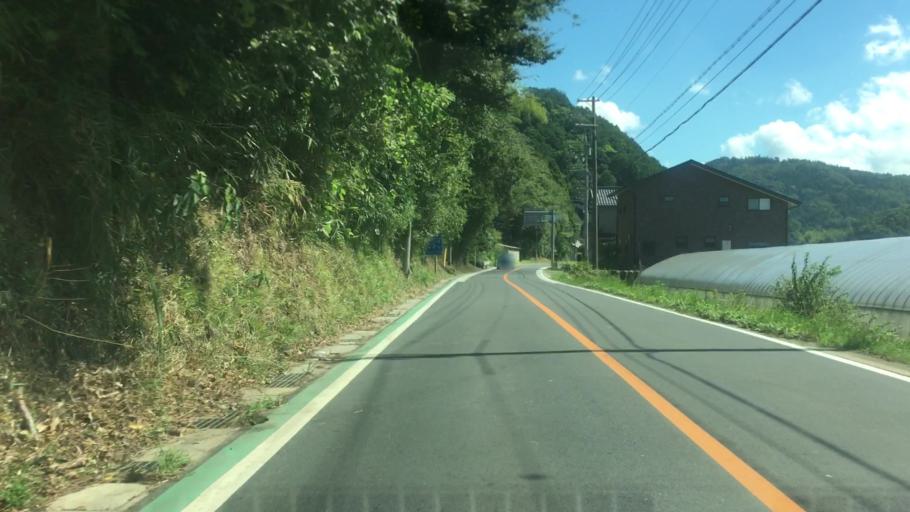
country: JP
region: Hyogo
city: Toyooka
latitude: 35.5986
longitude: 134.9043
